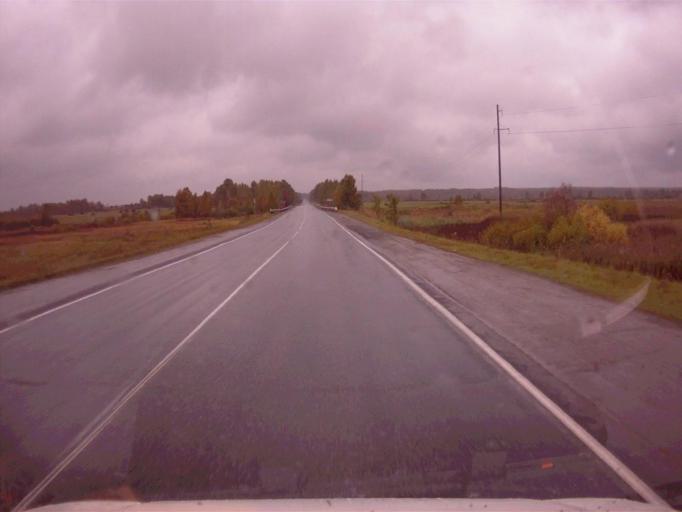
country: RU
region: Chelyabinsk
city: Argayash
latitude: 55.4793
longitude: 60.8106
